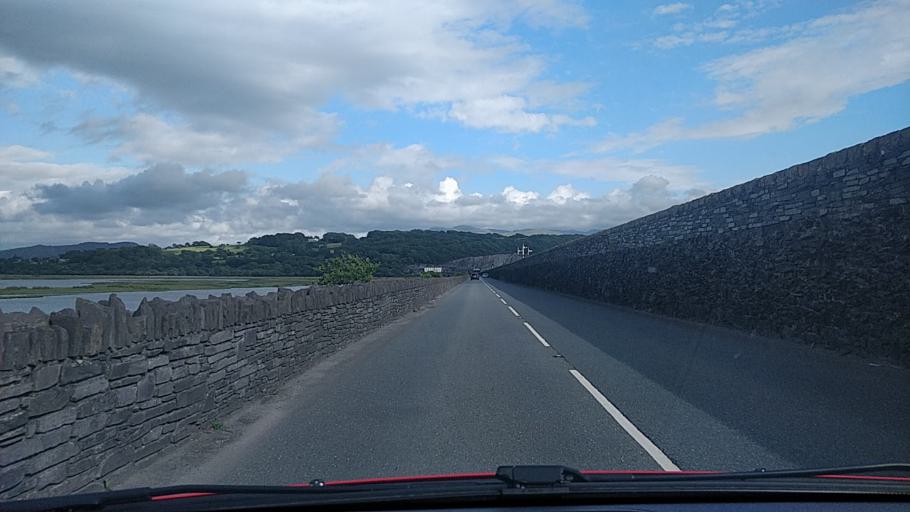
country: GB
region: Wales
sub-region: Gwynedd
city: Porthmadog
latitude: 52.9227
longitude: -4.1197
